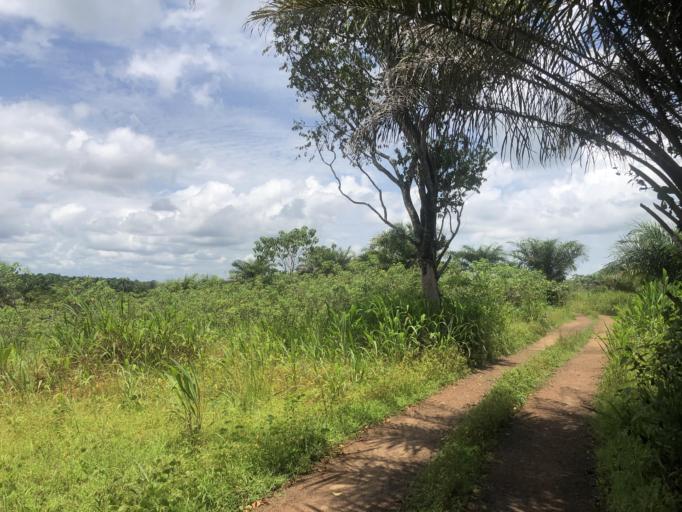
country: SL
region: Northern Province
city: Magburaka
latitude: 8.7091
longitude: -11.9411
